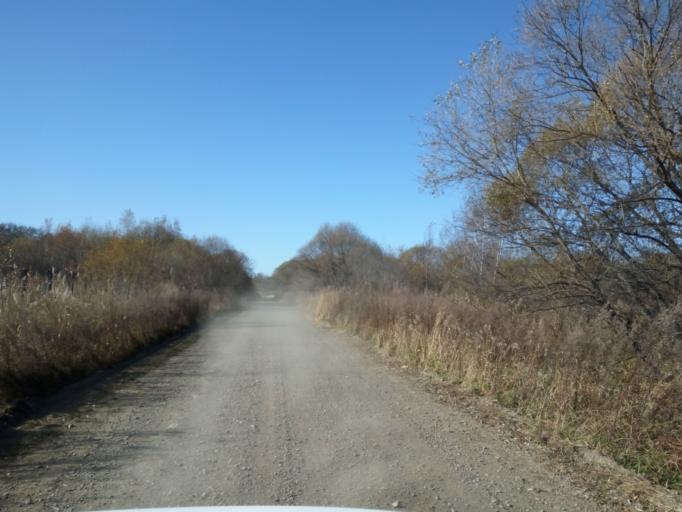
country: RU
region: Primorskiy
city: Dal'nerechensk
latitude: 45.9405
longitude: 133.6785
